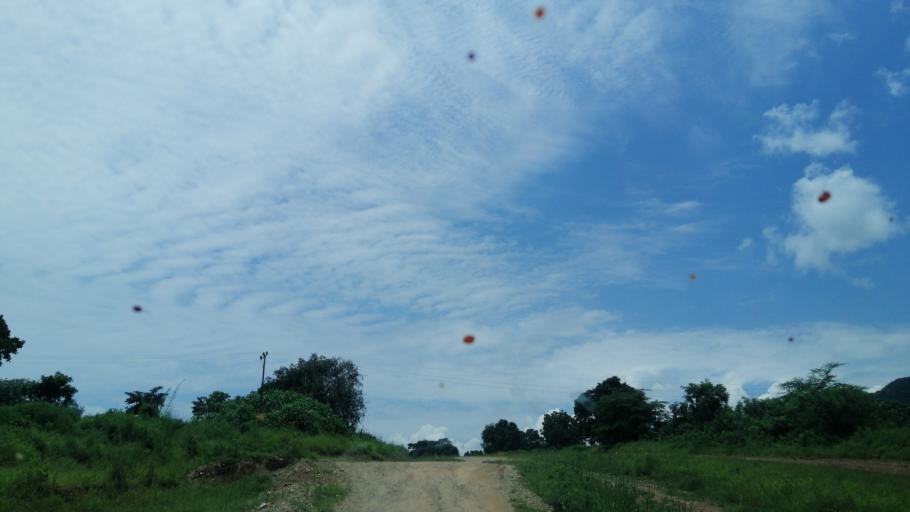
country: ET
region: Oromiya
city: Mendi
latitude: 10.1685
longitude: 35.0920
